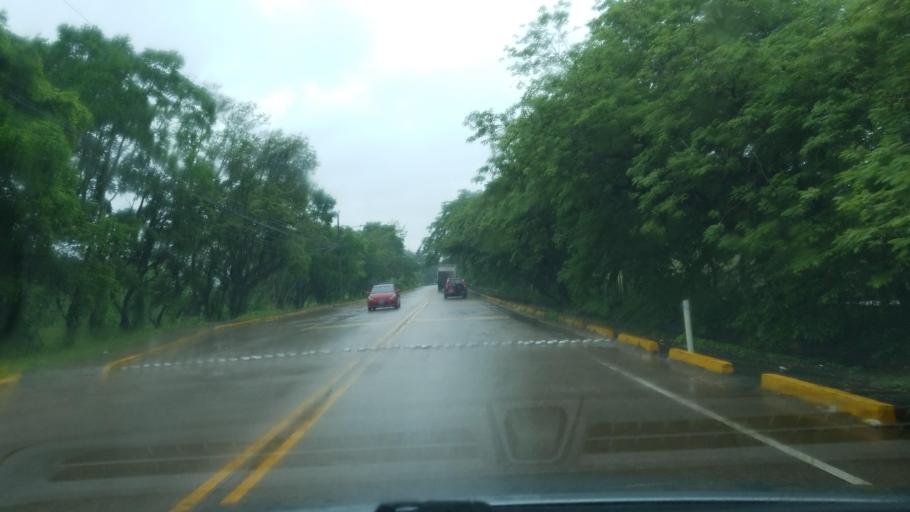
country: HN
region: Copan
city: Copan
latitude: 14.8395
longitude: -89.1480
